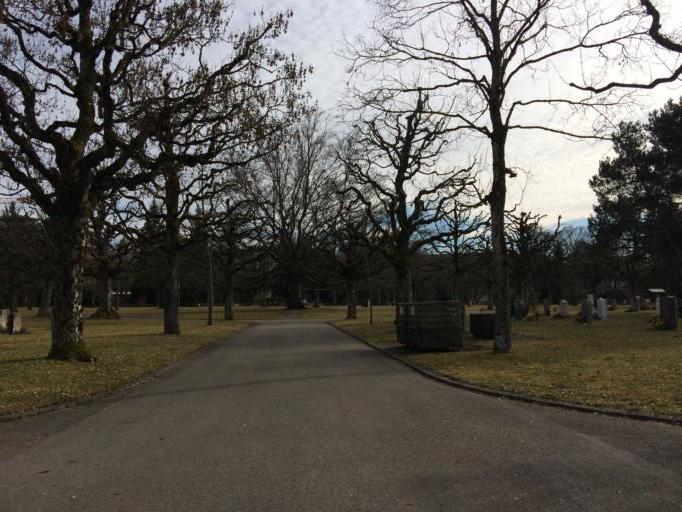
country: CH
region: Bern
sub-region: Bern-Mittelland District
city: Koniz
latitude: 46.9488
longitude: 7.4202
